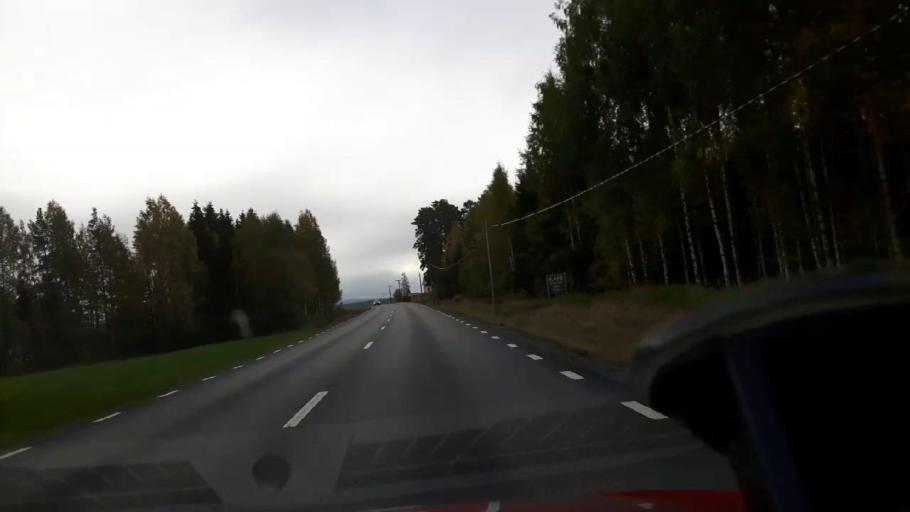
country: SE
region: Gaevleborg
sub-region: Ljusdals Kommun
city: Farila
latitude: 61.8692
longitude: 15.7289
